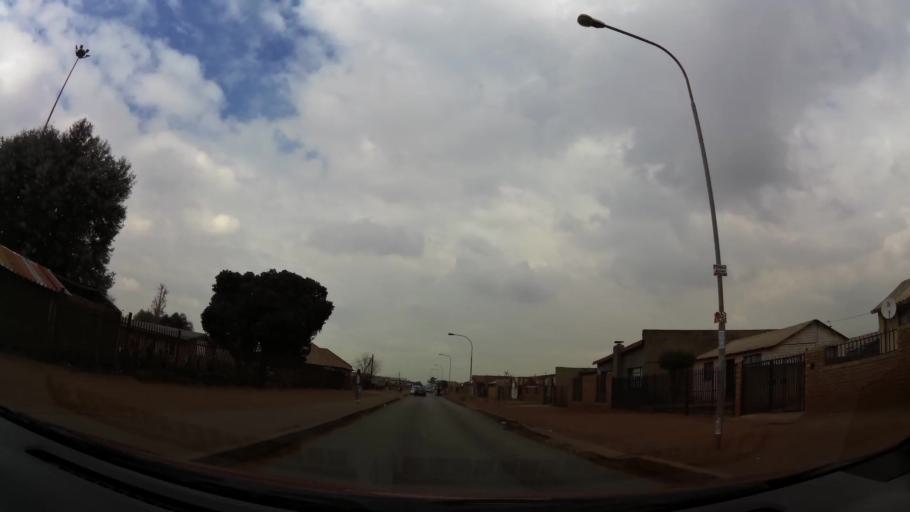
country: ZA
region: Gauteng
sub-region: City of Johannesburg Metropolitan Municipality
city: Soweto
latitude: -26.2557
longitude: 27.8327
